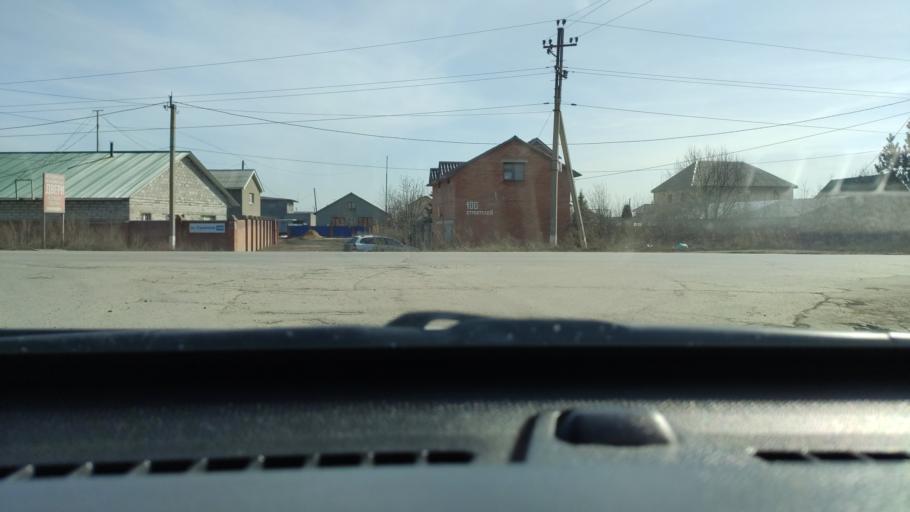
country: RU
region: Samara
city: Tol'yatti
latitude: 53.5619
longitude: 49.3979
